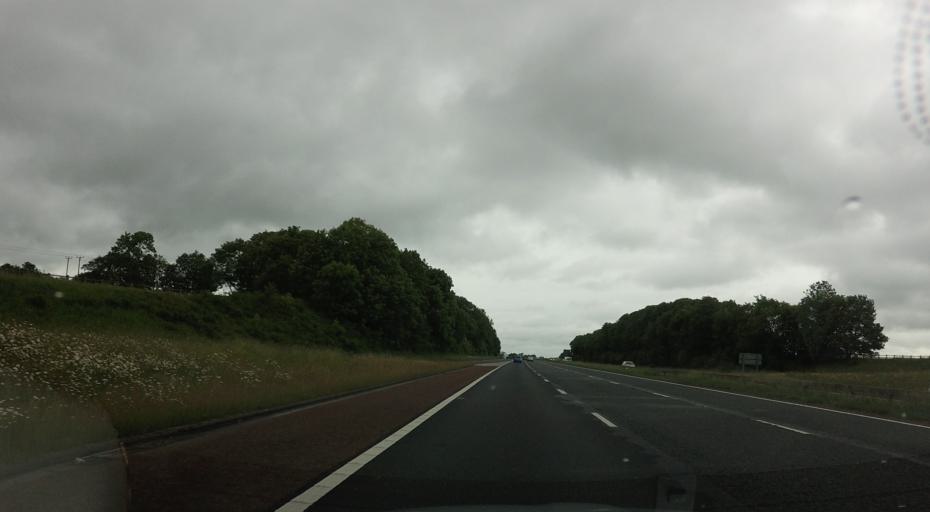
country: GB
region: England
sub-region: Cumbria
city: Penrith
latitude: 54.6951
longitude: -2.7919
